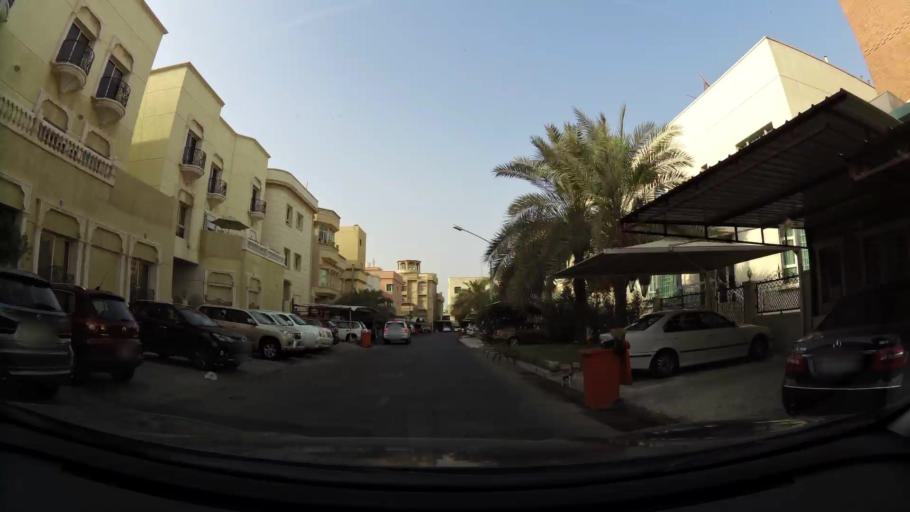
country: KW
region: Muhafazat Hawalli
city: Hawalli
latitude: 29.3196
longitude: 48.0013
